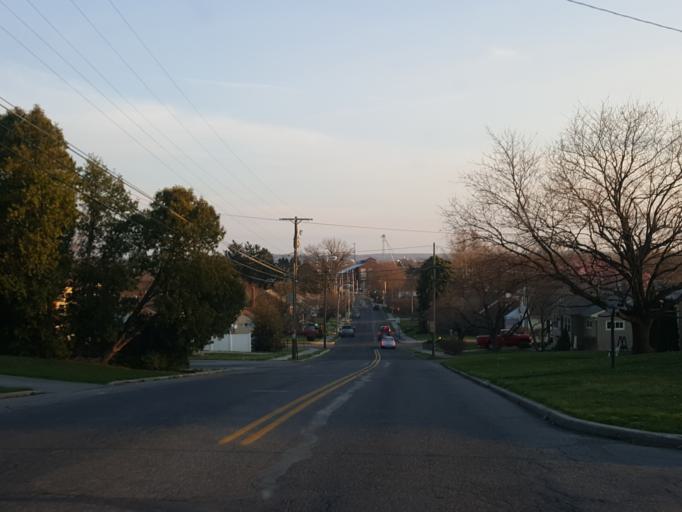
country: US
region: Pennsylvania
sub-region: Lebanon County
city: Avon
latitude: 40.3500
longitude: -76.3985
